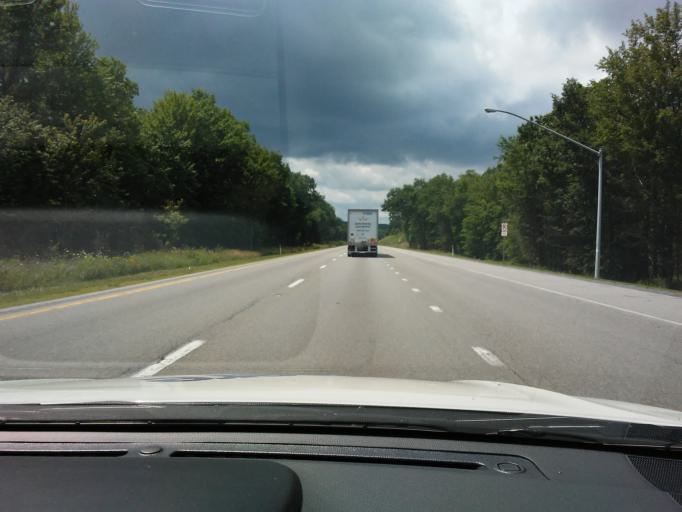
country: US
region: Pennsylvania
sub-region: Centre County
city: Milesburg
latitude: 41.0158
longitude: -77.9565
